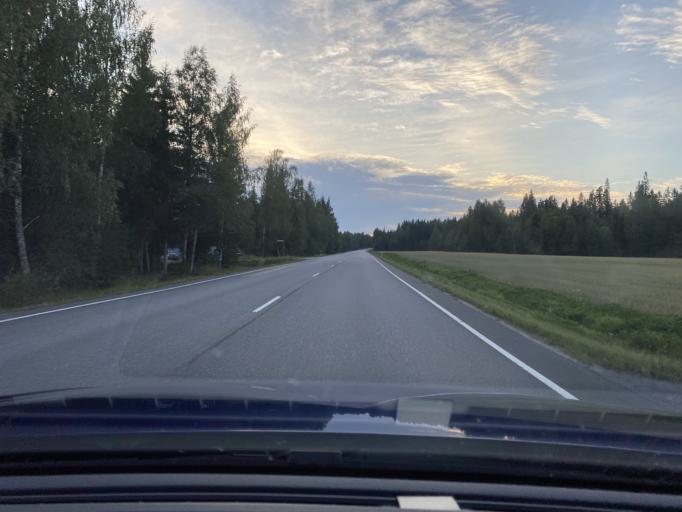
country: FI
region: Satakunta
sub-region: Pohjois-Satakunta
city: Kankaanpaeae
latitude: 61.7664
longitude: 22.4783
